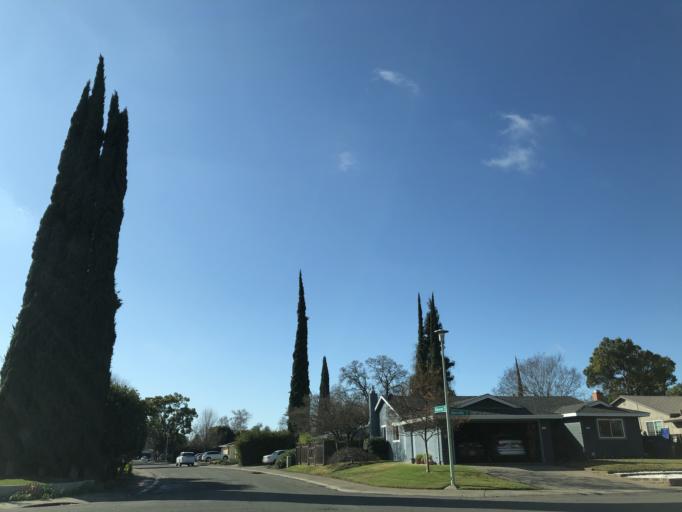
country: US
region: California
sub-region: Sacramento County
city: Rosemont
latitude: 38.5628
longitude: -121.3850
